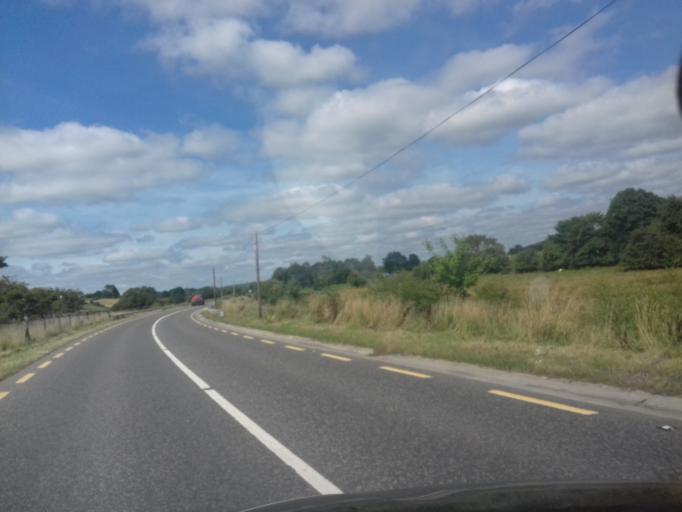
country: IE
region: Leinster
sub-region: Wicklow
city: Valleymount
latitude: 53.0411
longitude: -6.6360
